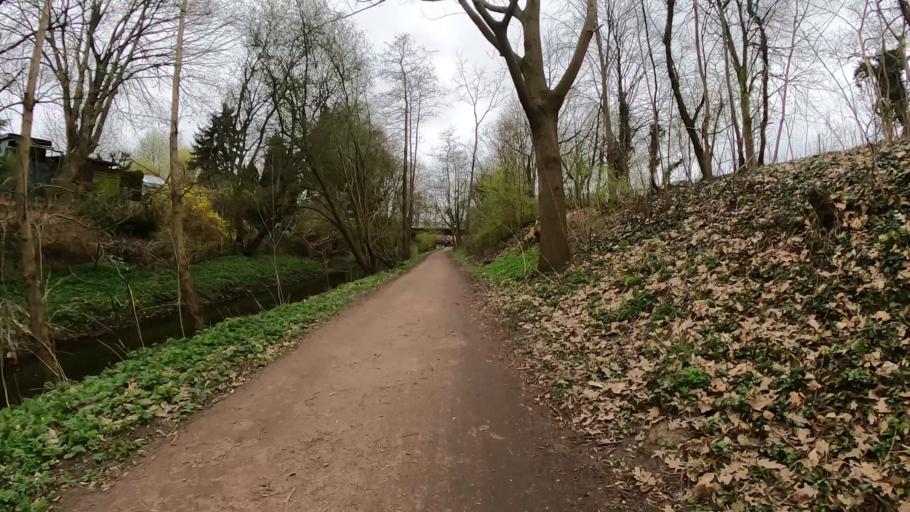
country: DE
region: Hamburg
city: Hamburg-Nord
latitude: 53.6142
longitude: 9.9671
